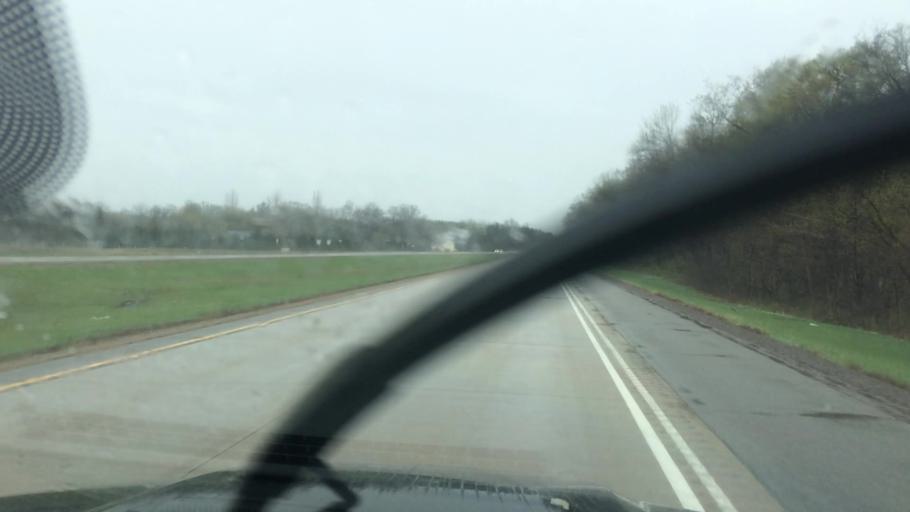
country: US
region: Wisconsin
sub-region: Portage County
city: Stevens Point
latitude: 44.6473
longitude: -89.6375
